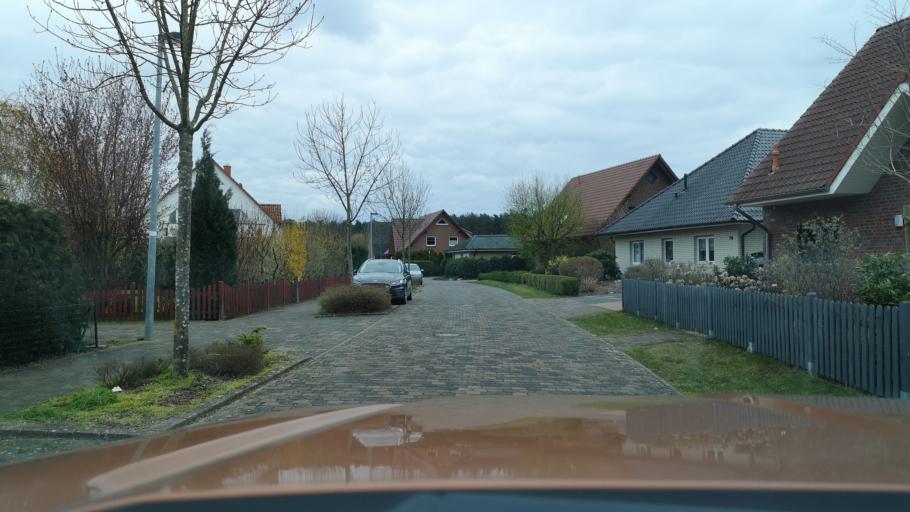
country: DE
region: Lower Saxony
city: Hambuhren
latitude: 52.6231
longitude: 9.9691
